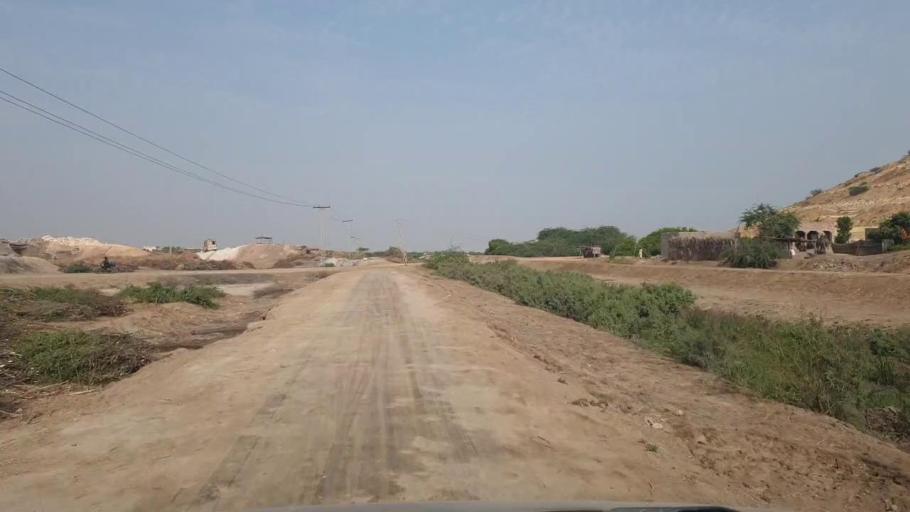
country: PK
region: Sindh
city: Tando Muhammad Khan
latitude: 25.1361
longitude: 68.4563
